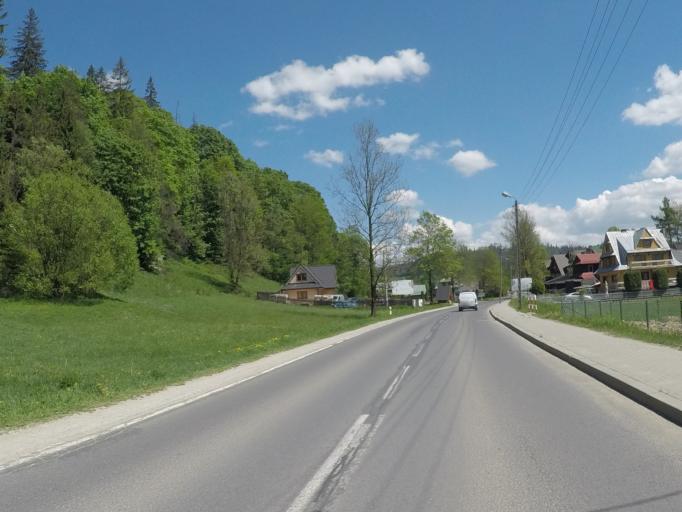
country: PL
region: Lesser Poland Voivodeship
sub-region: Powiat tatrzanski
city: Poronin
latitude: 49.3315
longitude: 20.0240
